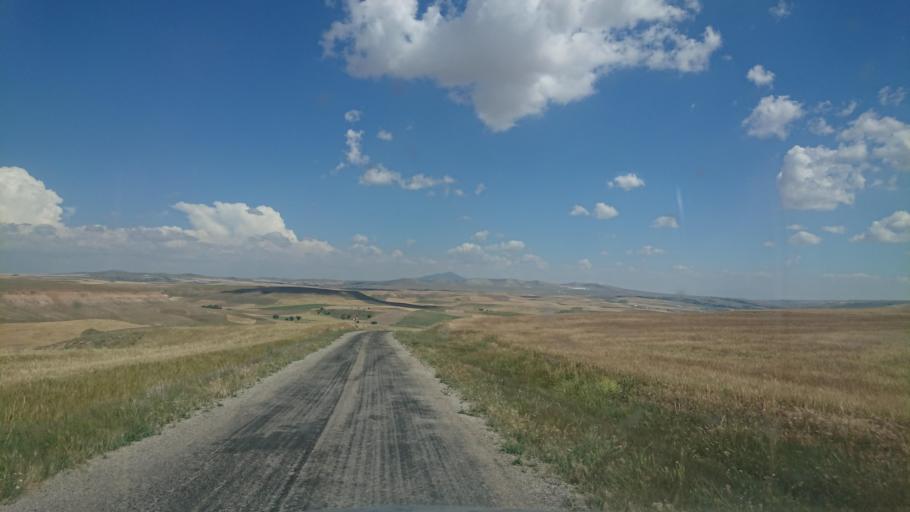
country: TR
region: Aksaray
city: Agacoren
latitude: 38.8058
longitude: 33.8097
